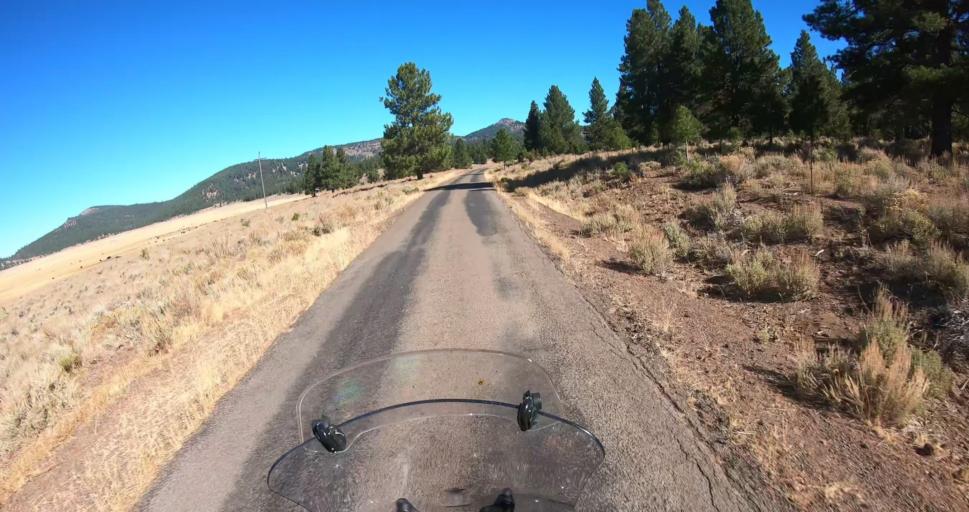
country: US
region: Oregon
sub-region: Lake County
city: Lakeview
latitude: 42.2084
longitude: -120.2550
